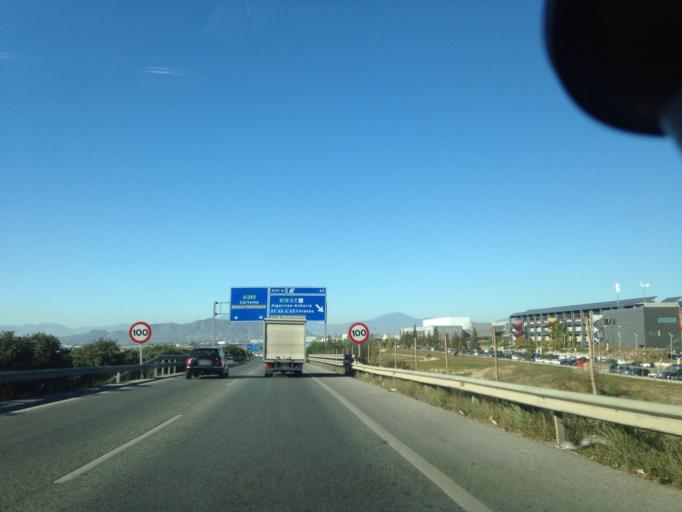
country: ES
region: Andalusia
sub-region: Provincia de Malaga
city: Malaga
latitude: 36.7141
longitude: -4.4899
